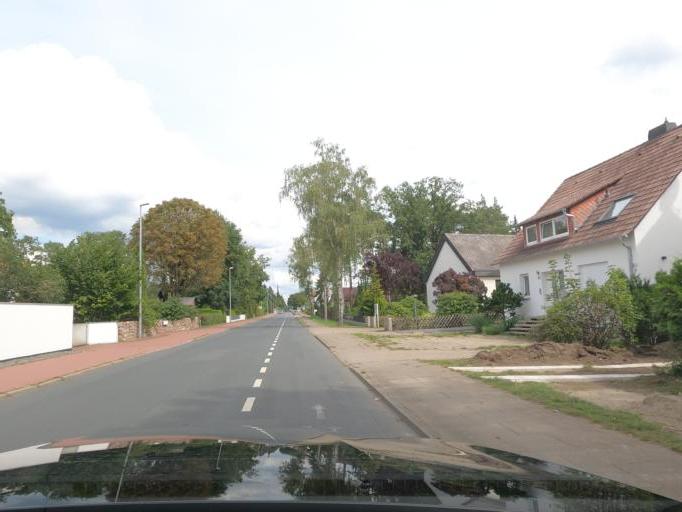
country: DE
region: Lower Saxony
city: Adelheidsdorf
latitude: 52.5160
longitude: 10.0111
